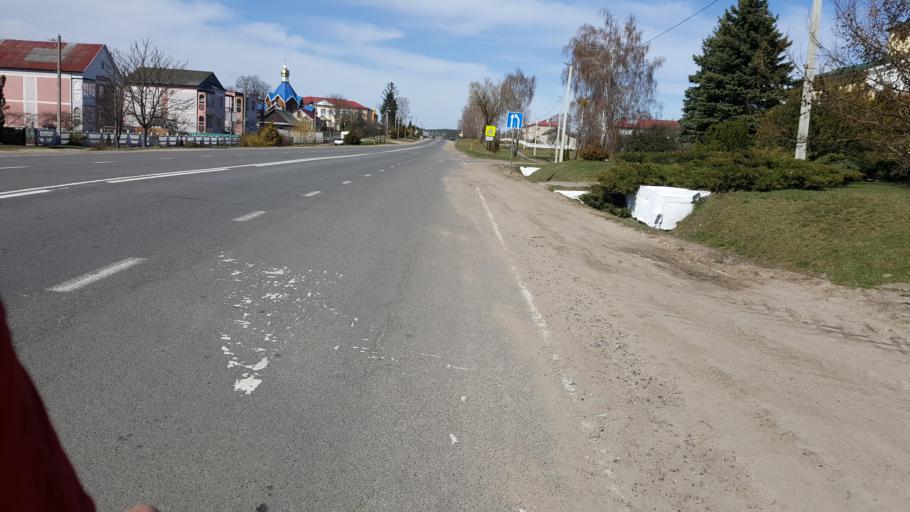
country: BY
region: Brest
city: Kamyanyets
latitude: 52.3270
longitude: 23.7829
